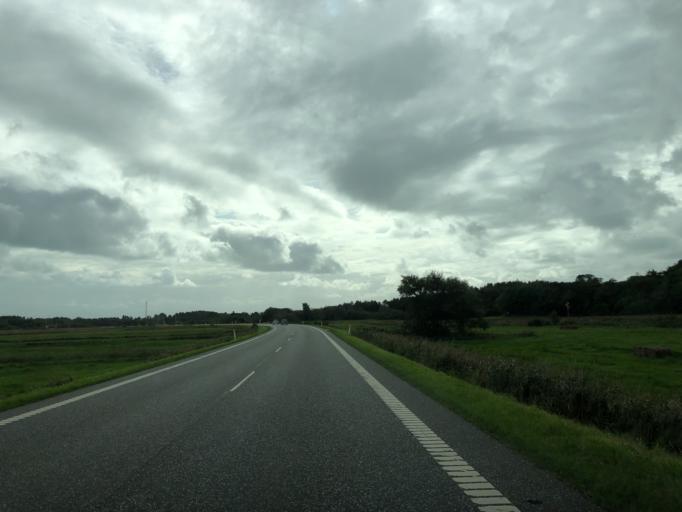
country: DK
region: North Denmark
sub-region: Thisted Kommune
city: Hurup
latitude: 56.6861
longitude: 8.3970
